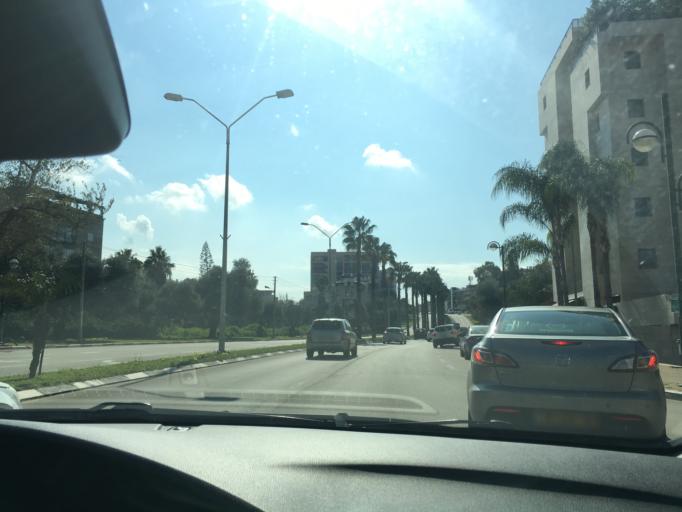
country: IL
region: Tel Aviv
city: Ramat HaSharon
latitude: 32.1516
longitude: 34.8419
